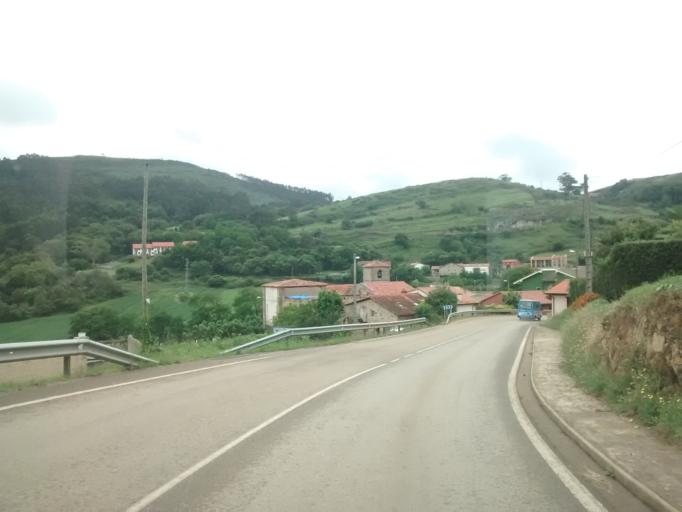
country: ES
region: Cantabria
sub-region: Provincia de Cantabria
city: Santillana
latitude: 43.4152
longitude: -4.1000
